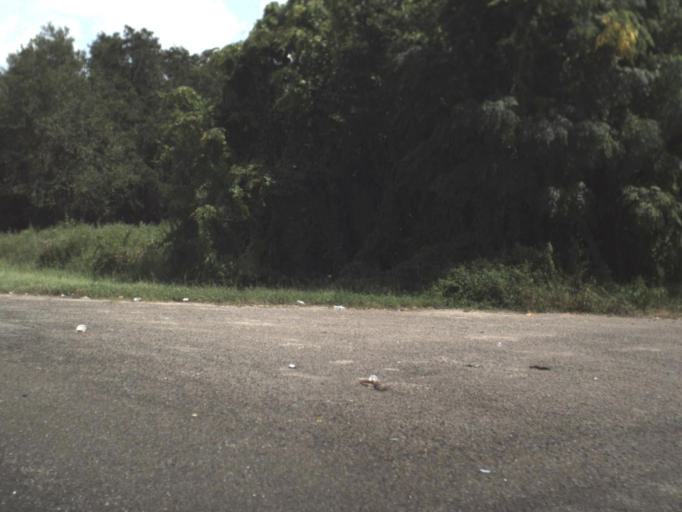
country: US
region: Florida
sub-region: Hillsborough County
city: Valrico
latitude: 27.9376
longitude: -82.2108
